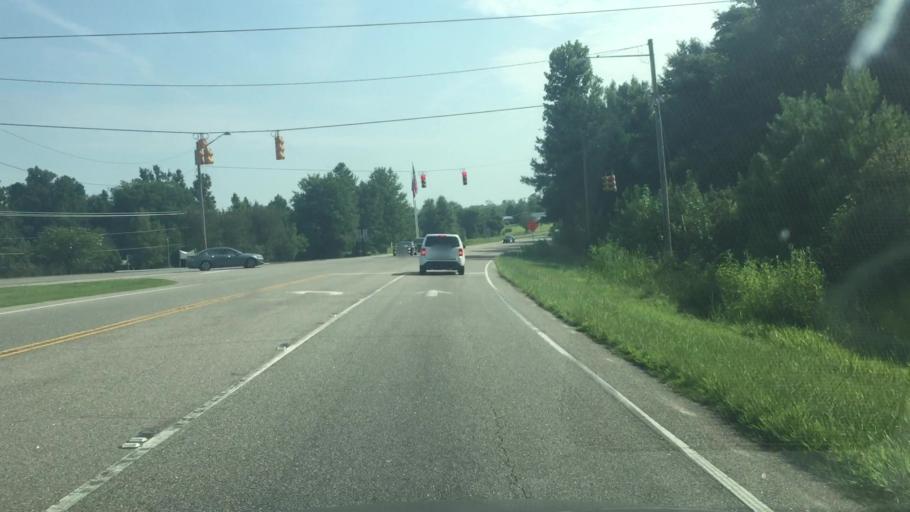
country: US
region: North Carolina
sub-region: Columbus County
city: Tabor City
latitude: 34.1561
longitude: -78.8583
